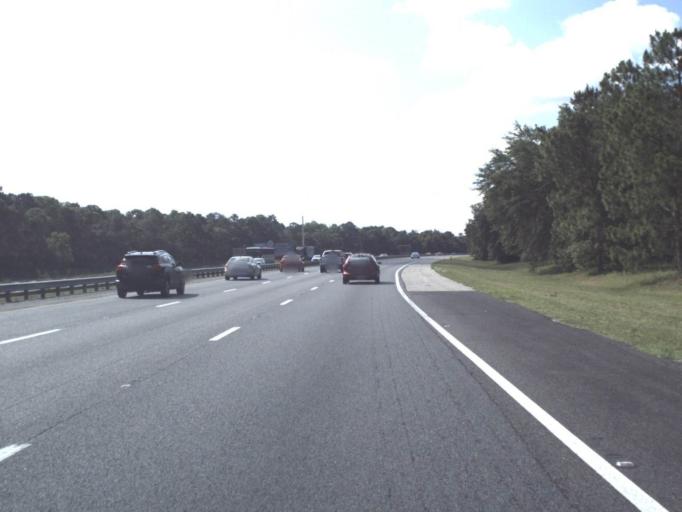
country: US
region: Florida
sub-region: Flagler County
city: Palm Coast
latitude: 29.6586
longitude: -81.2817
